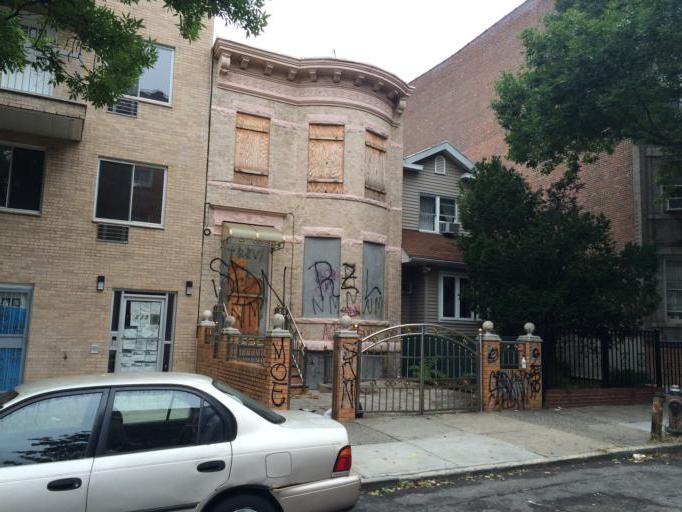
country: US
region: New York
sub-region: Kings County
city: Bensonhurst
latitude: 40.6458
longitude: -74.0189
